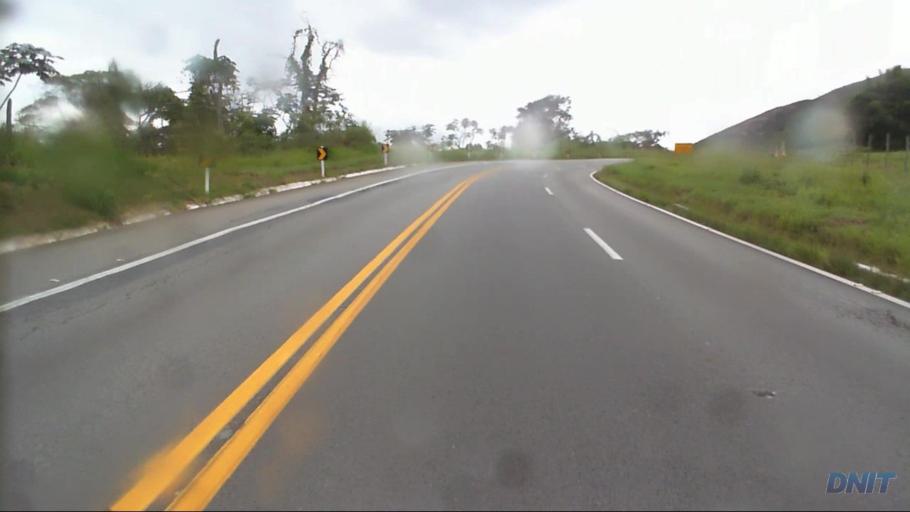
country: BR
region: Minas Gerais
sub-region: Nova Era
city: Nova Era
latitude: -19.6781
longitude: -42.9795
